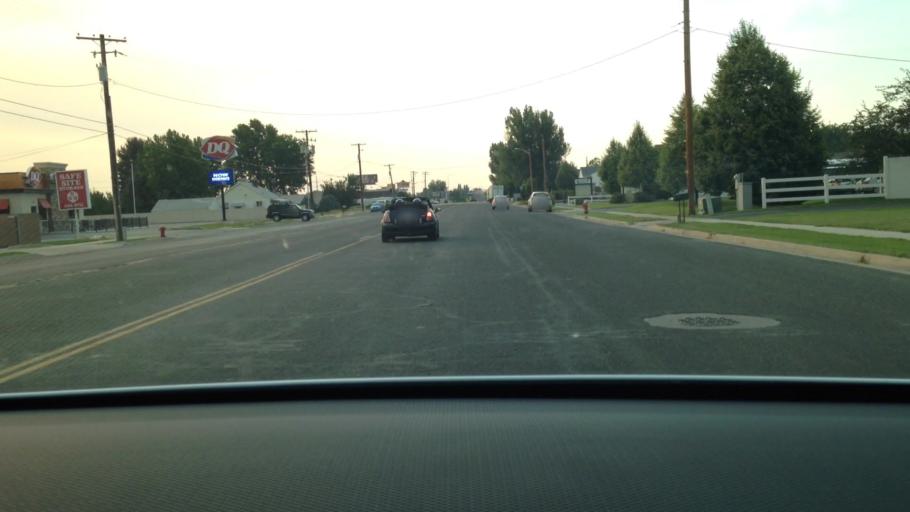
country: US
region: Utah
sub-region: Davis County
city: Layton
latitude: 41.0478
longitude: -111.9549
